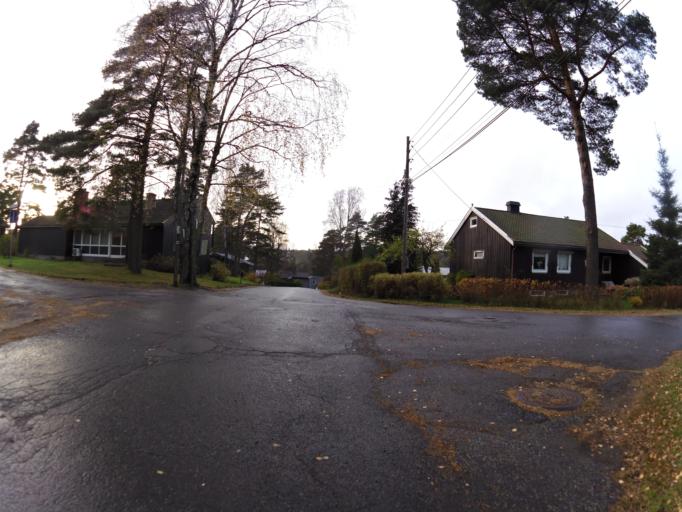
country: NO
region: Ostfold
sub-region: Fredrikstad
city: Fredrikstad
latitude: 59.2278
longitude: 10.9638
